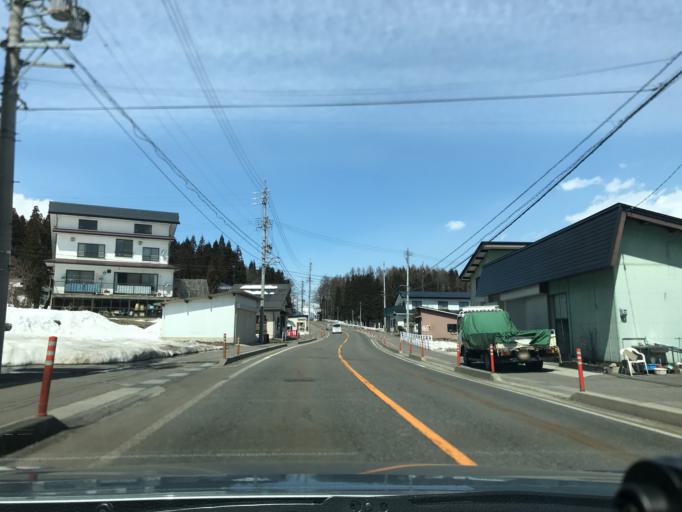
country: JP
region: Nagano
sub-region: Kitaazumi Gun
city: Hakuba
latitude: 36.6353
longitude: 137.8447
